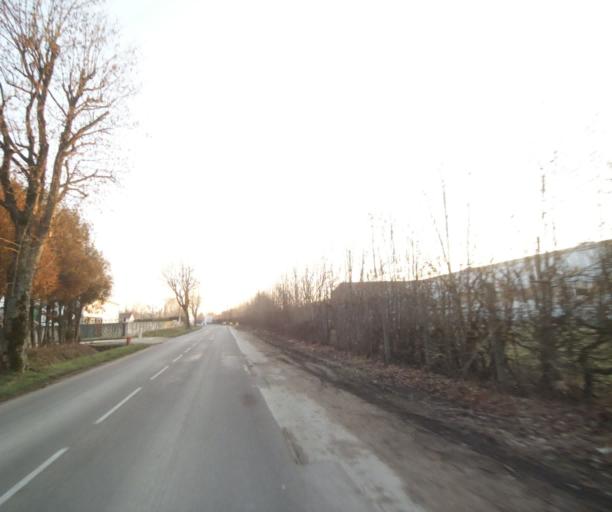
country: FR
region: Champagne-Ardenne
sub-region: Departement de la Haute-Marne
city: Bienville
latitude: 48.6001
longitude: 5.0436
